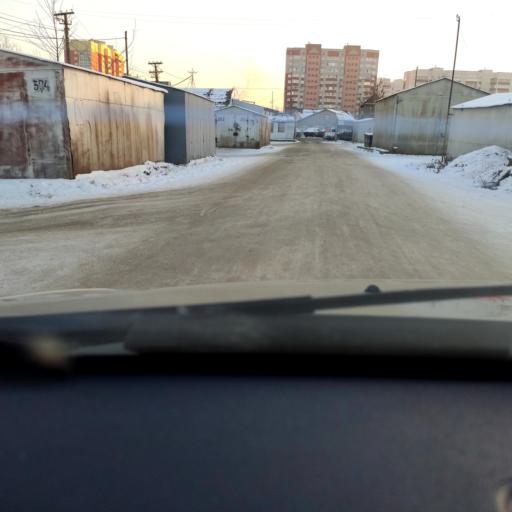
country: RU
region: Bashkortostan
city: Mikhaylovka
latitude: 54.7160
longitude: 55.8286
